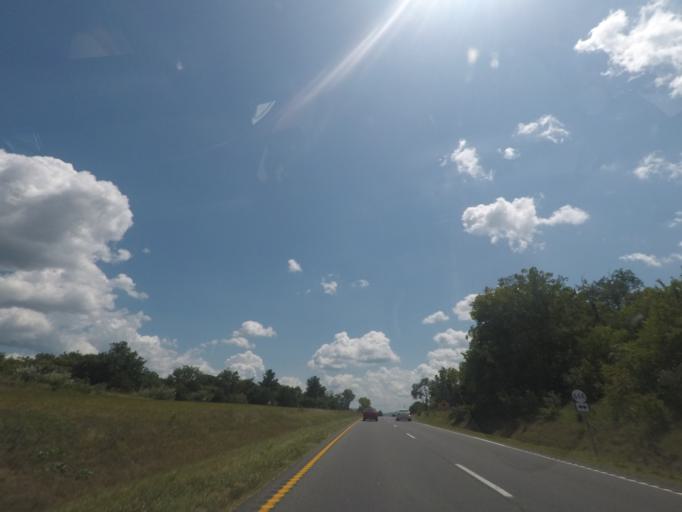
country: US
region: Virginia
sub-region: City of Winchester
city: Winchester
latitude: 39.0939
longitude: -78.1020
